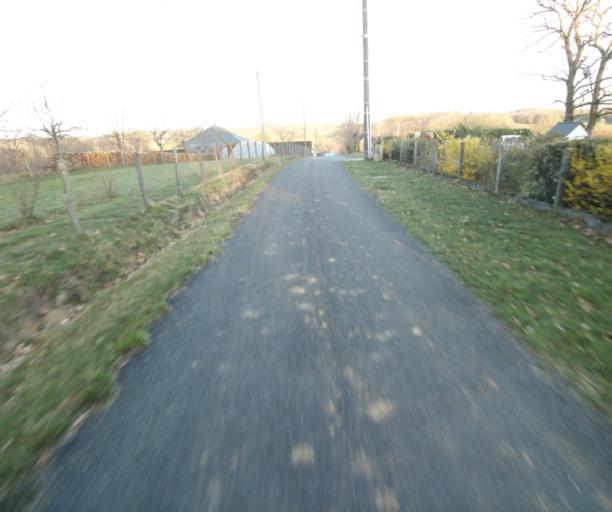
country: FR
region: Limousin
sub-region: Departement de la Correze
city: Uzerche
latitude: 45.3660
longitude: 1.6066
